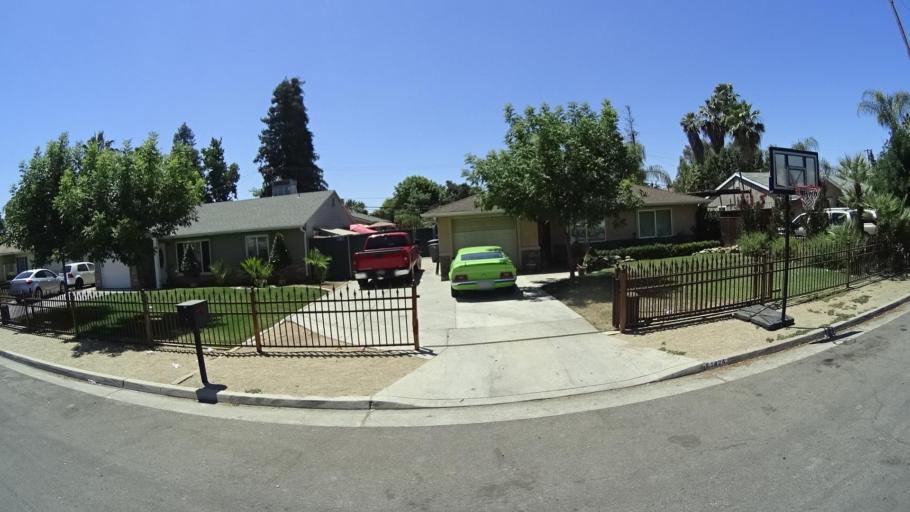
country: US
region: California
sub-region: Fresno County
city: Fresno
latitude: 36.7914
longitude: -119.7934
